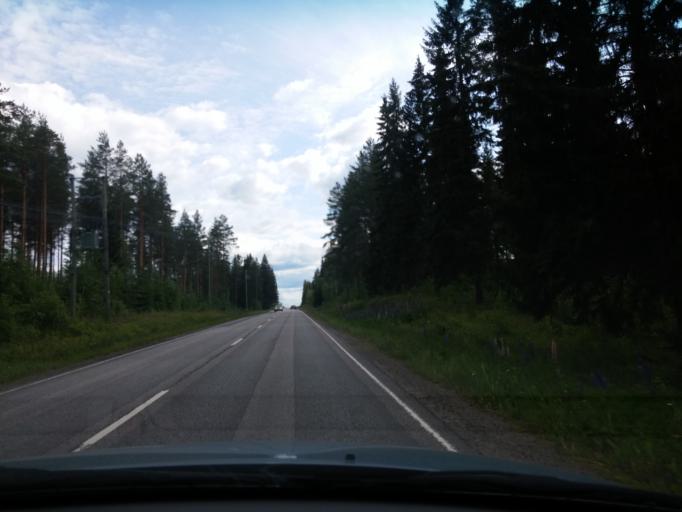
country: FI
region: Central Finland
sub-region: Keuruu
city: Keuruu
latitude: 62.3302
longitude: 24.7328
